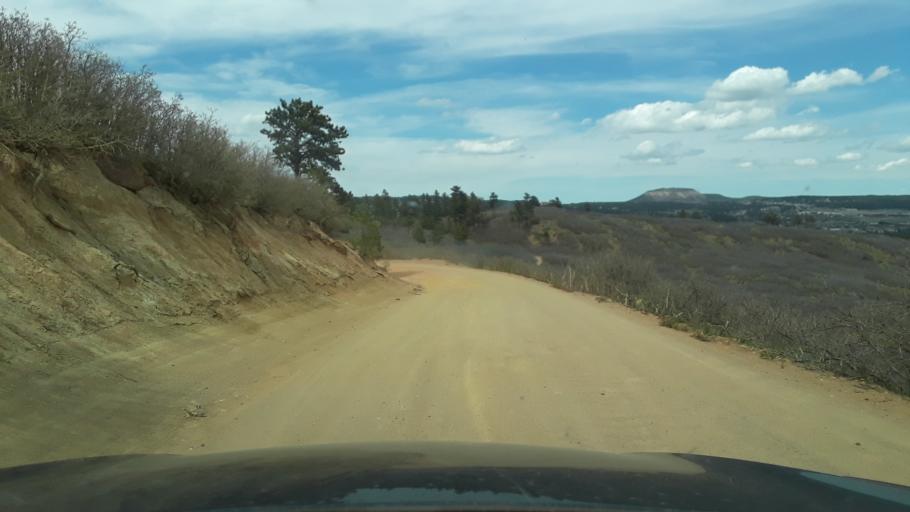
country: US
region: Colorado
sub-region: El Paso County
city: Palmer Lake
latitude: 39.0847
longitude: -104.9120
